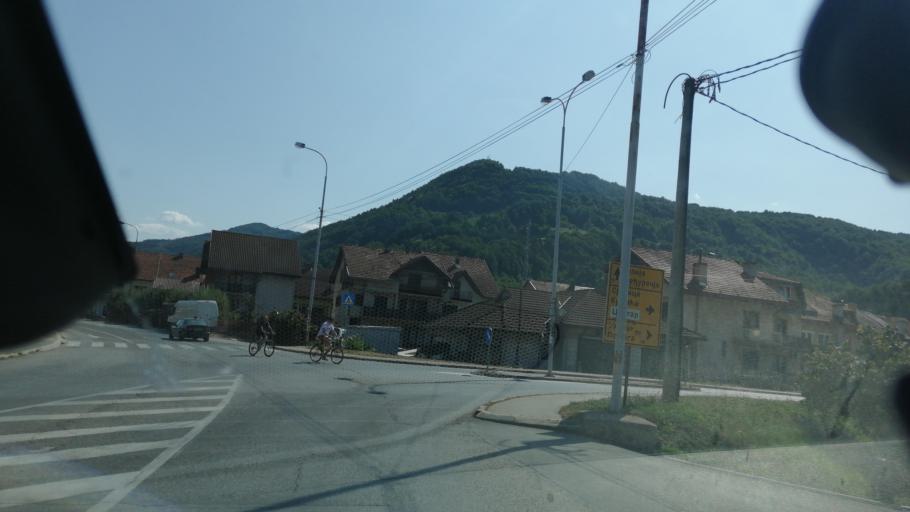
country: RS
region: Central Serbia
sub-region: Moravicki Okrug
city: Ivanjica
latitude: 43.5987
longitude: 20.2237
